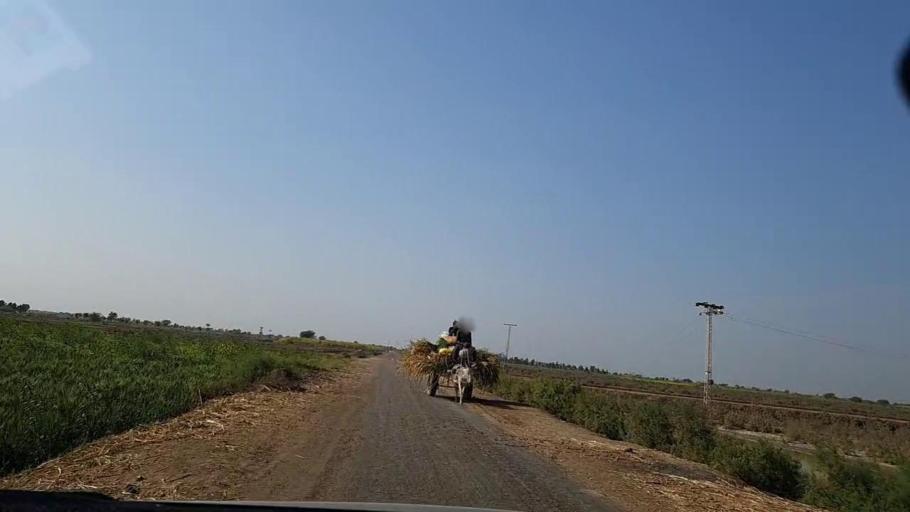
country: PK
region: Sindh
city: Digri
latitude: 25.1681
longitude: 69.0221
